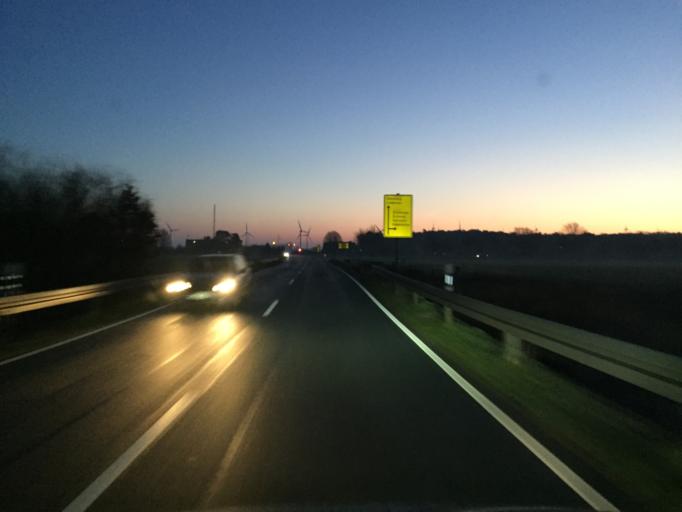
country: DE
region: Lower Saxony
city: Steyerberg
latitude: 52.5609
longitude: 9.0255
